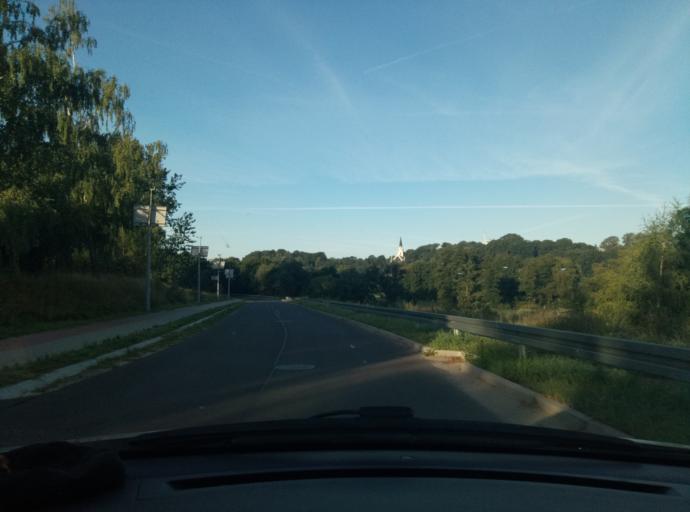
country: PL
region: Kujawsko-Pomorskie
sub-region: Powiat brodnicki
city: Jablonowo Pomorskie
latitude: 53.3896
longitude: 19.1444
